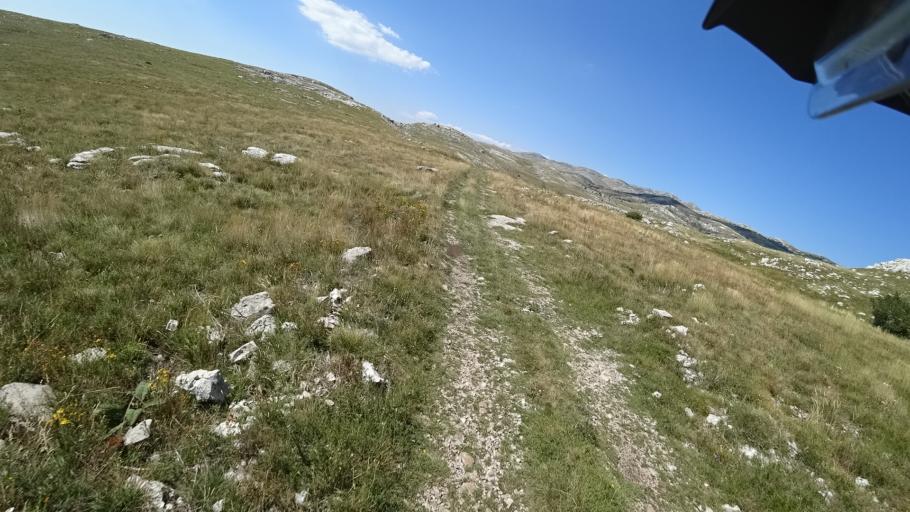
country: HR
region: Splitsko-Dalmatinska
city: Hrvace
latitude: 43.8955
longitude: 16.6285
